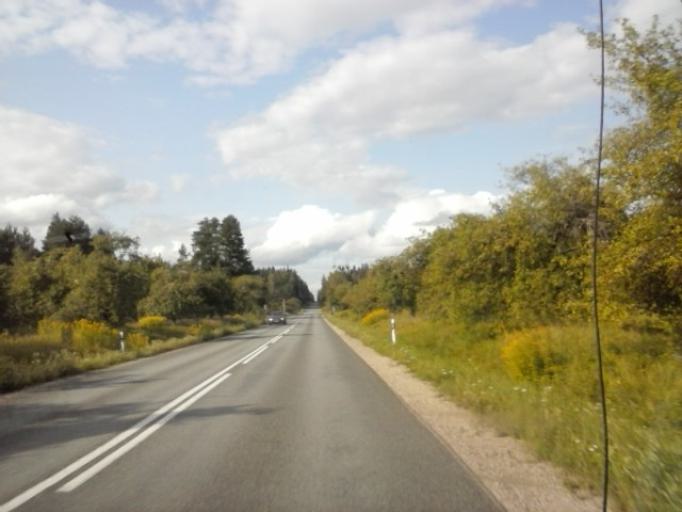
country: LV
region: Valmieras Rajons
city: Valmiera
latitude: 57.4825
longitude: 25.4092
